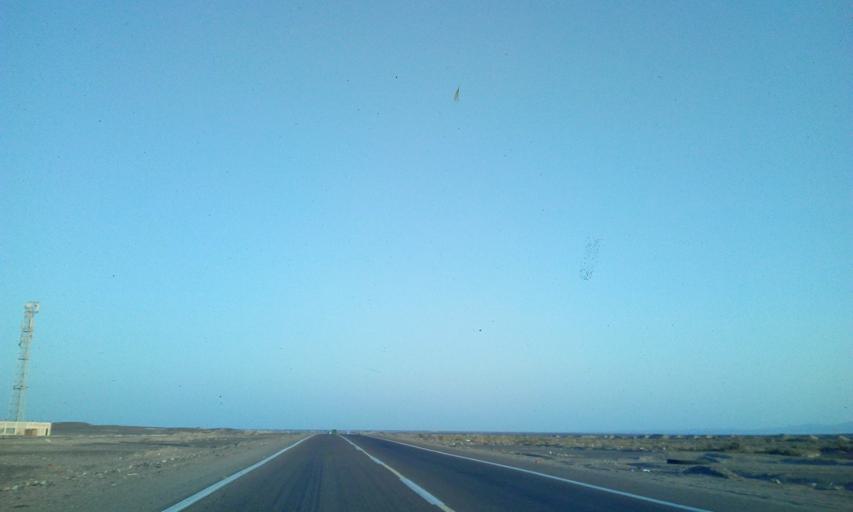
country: EG
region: South Sinai
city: Tor
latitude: 28.0220
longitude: 33.3043
